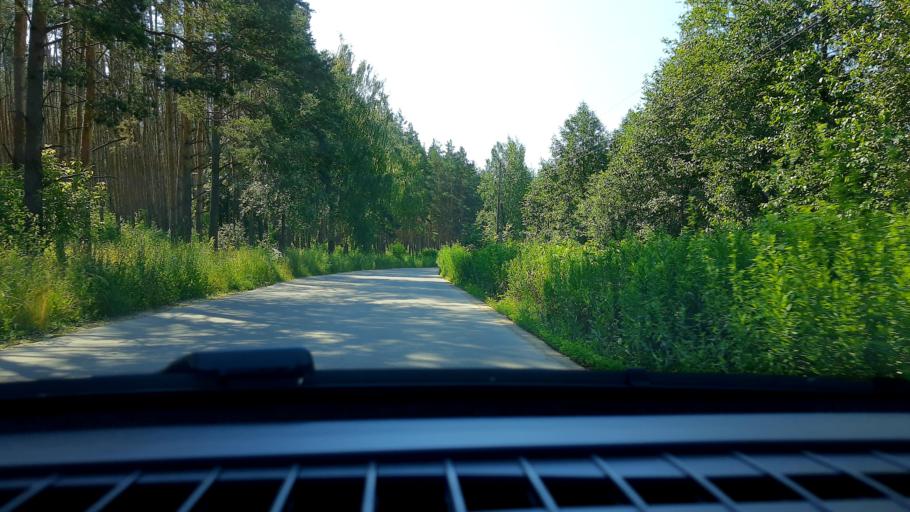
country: RU
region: Nizjnij Novgorod
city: Gorbatovka
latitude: 56.2285
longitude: 43.7628
